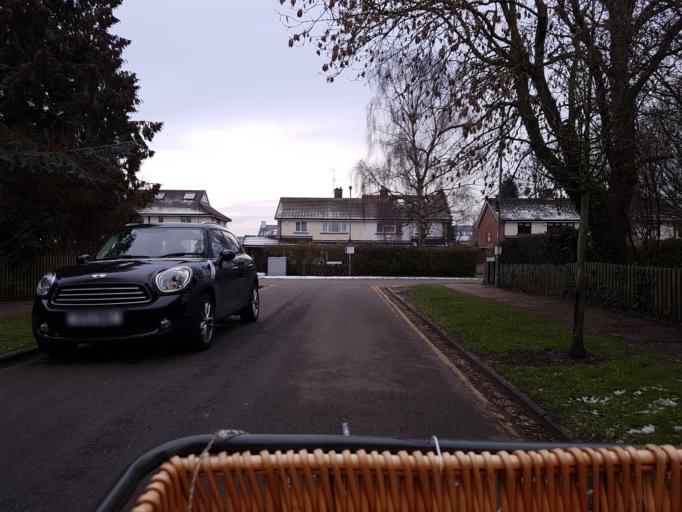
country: GB
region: England
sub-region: Cambridgeshire
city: Cambridge
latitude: 52.1829
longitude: 0.1455
